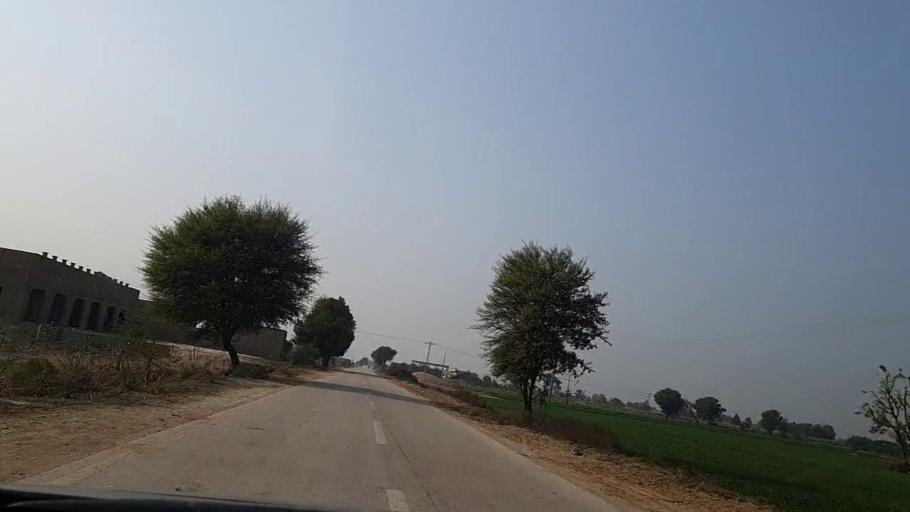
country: PK
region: Sindh
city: Sann
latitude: 26.1435
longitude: 68.1485
